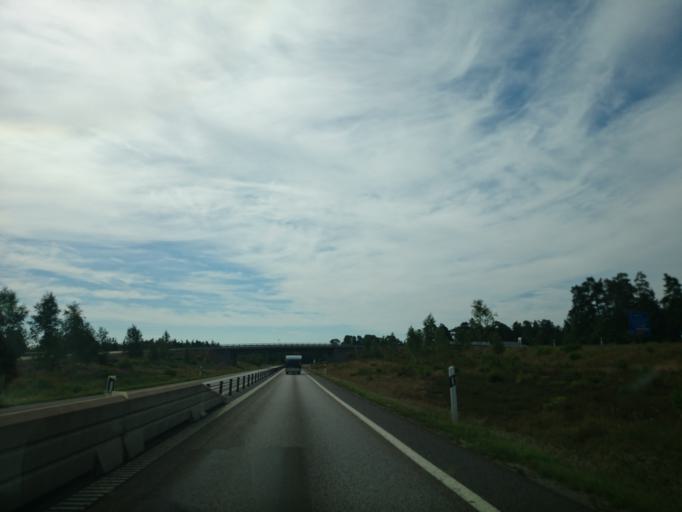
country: SE
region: Kalmar
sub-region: Oskarshamns Kommun
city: Oskarshamn
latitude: 57.3742
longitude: 16.4882
